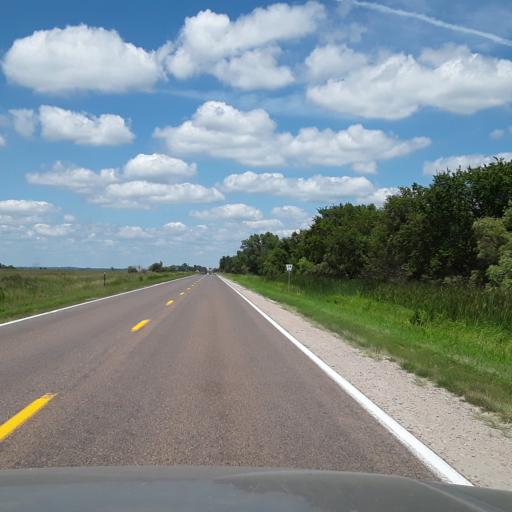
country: US
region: Nebraska
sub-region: Nance County
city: Genoa
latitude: 41.3522
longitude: -97.6950
